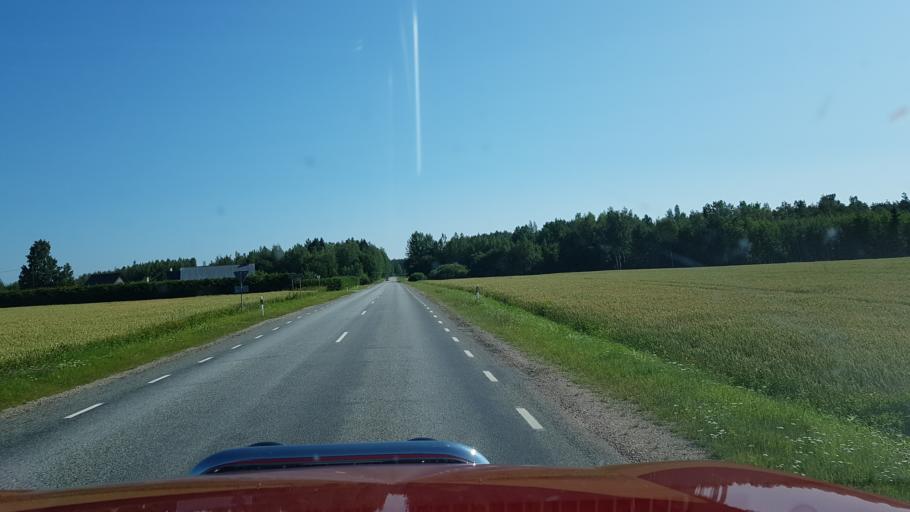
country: EE
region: Polvamaa
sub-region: Polva linn
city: Polva
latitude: 58.0010
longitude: 26.9326
